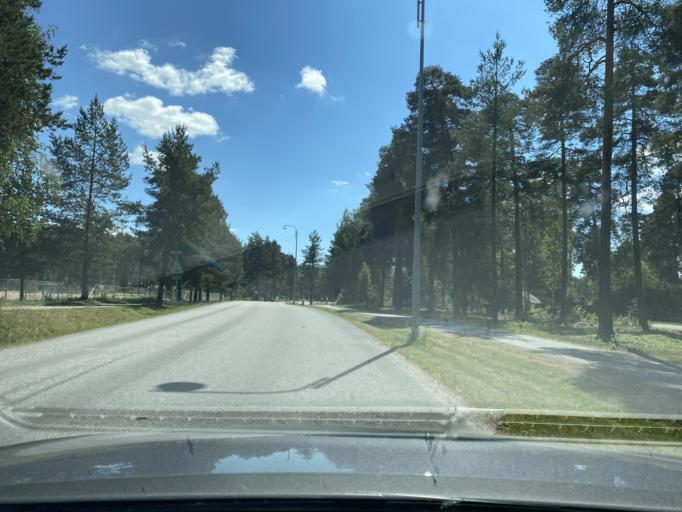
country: FI
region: Satakunta
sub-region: Rauma
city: Eura
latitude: 61.1194
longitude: 22.1599
